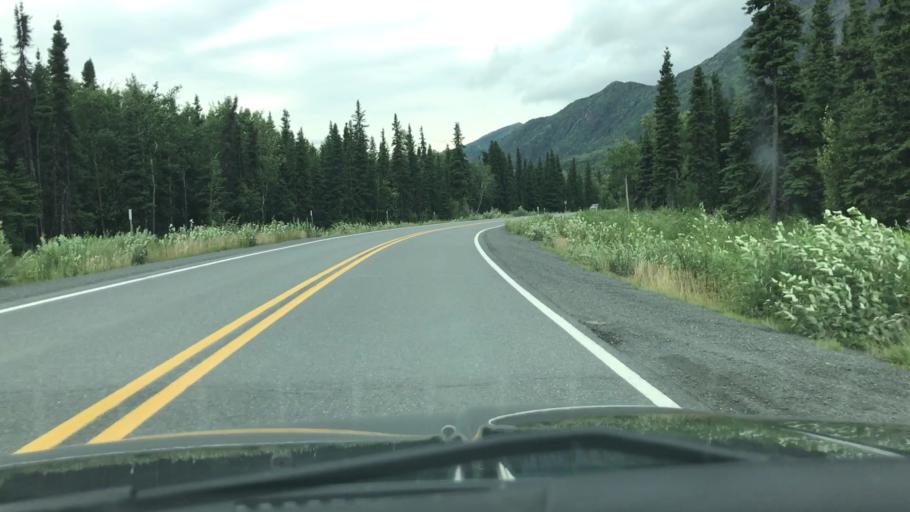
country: US
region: Alaska
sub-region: Kenai Peninsula Borough
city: Seward
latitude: 60.4836
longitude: -149.9561
